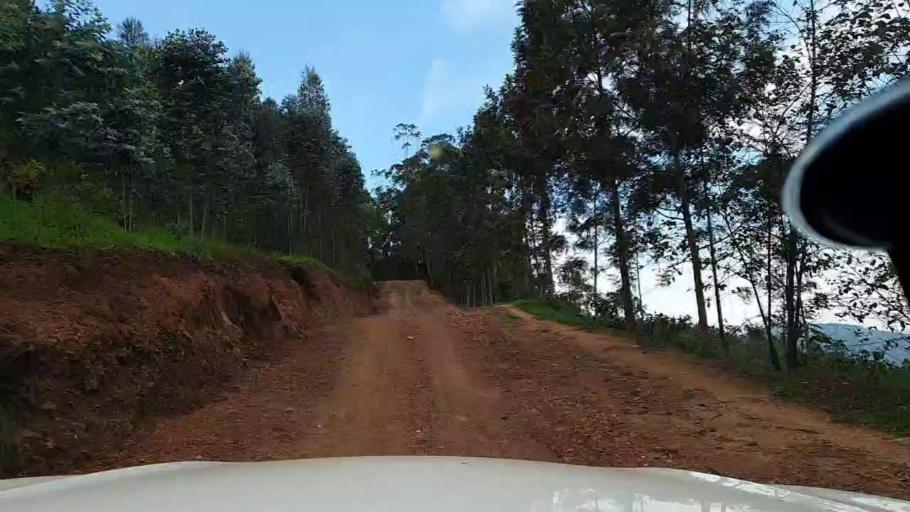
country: RW
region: Southern Province
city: Gitarama
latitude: -1.8062
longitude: 29.7987
